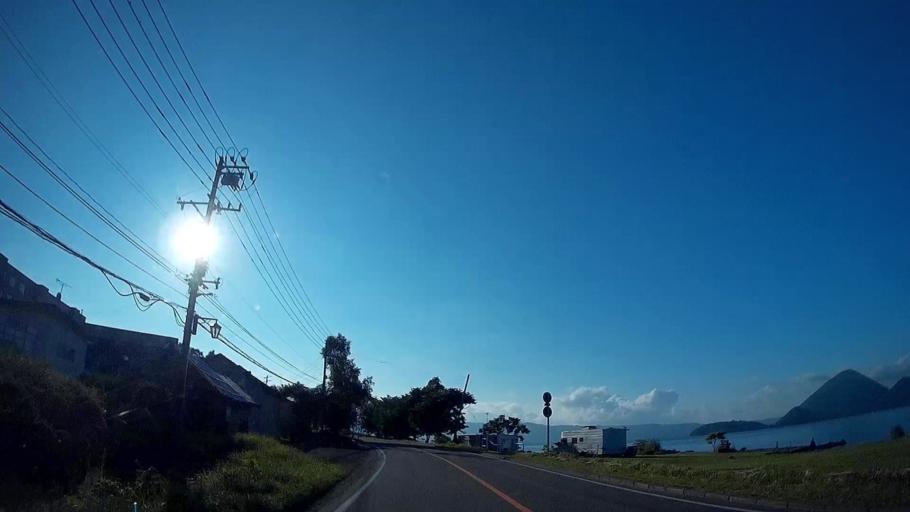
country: JP
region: Hokkaido
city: Date
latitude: 42.5632
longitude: 140.8451
